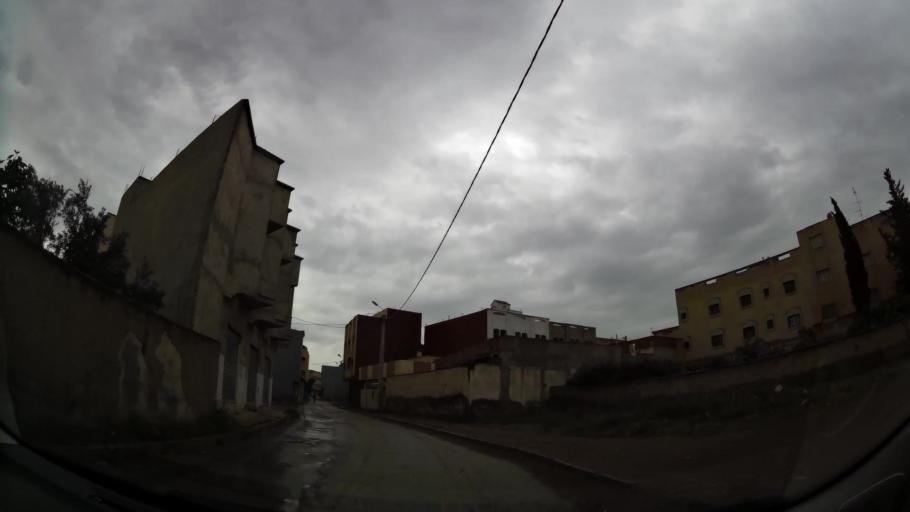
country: MA
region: Oriental
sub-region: Nador
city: Nador
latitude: 35.1499
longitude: -2.9986
